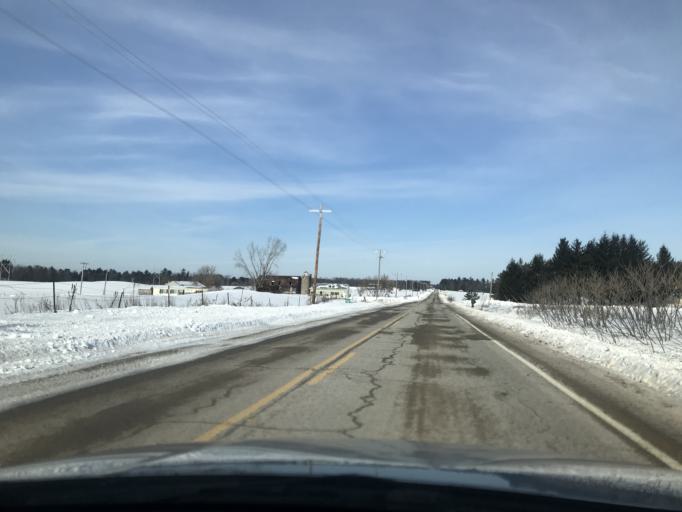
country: US
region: Wisconsin
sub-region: Oconto County
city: Oconto Falls
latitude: 45.1246
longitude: -88.1780
